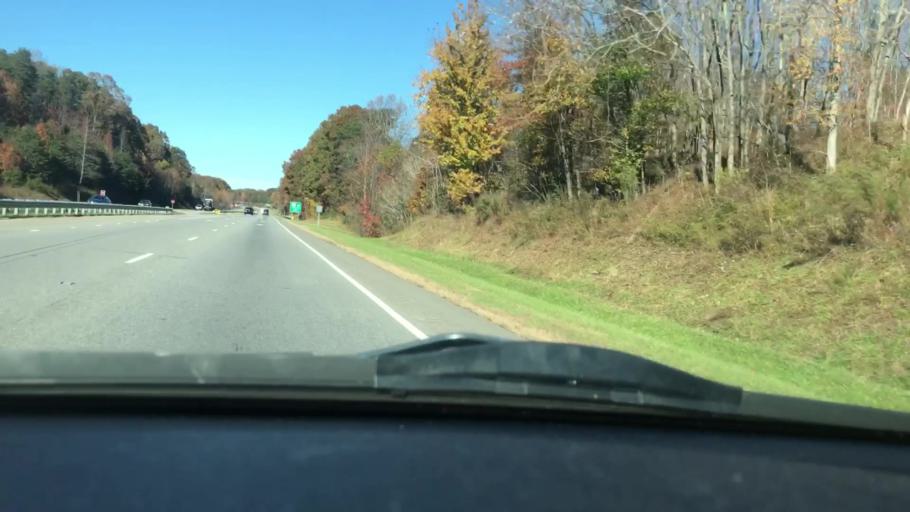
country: US
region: North Carolina
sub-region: Rockingham County
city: Madison
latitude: 36.3960
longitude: -79.9401
